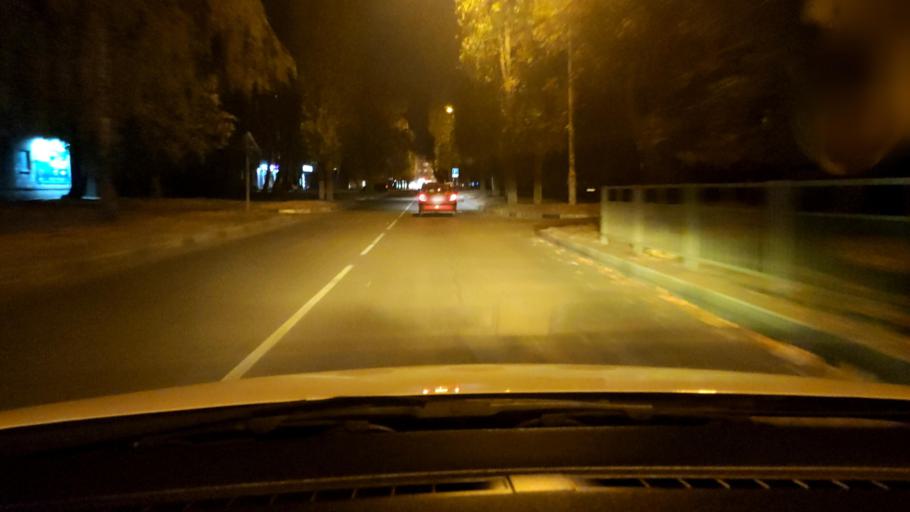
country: RU
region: Voronezj
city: Voronezh
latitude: 51.6563
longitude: 39.1522
